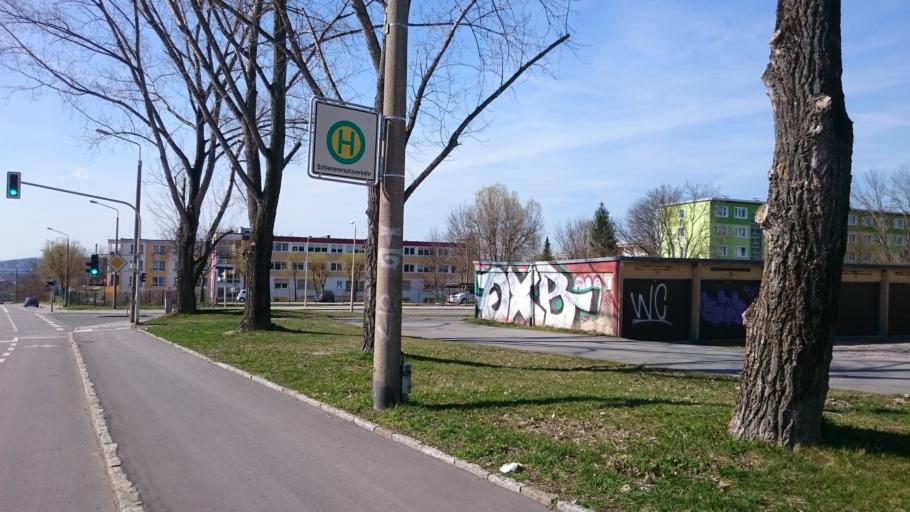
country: DE
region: Saxony
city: Zwickau
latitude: 50.7324
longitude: 12.5128
